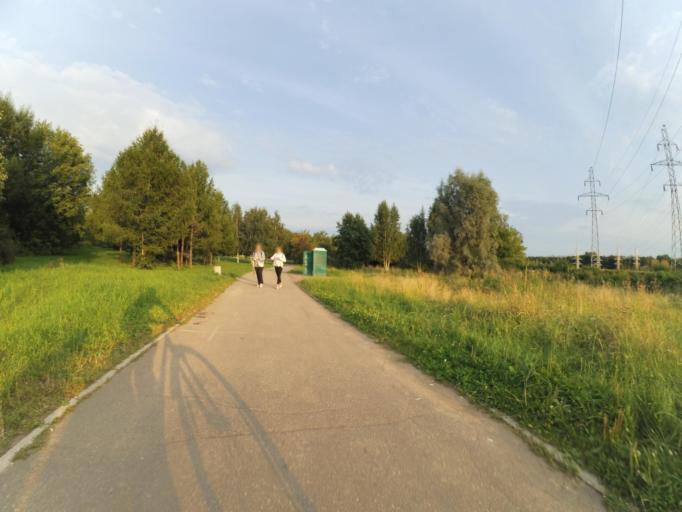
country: RU
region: Moscow
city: Lyublino
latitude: 55.6899
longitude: 37.7584
